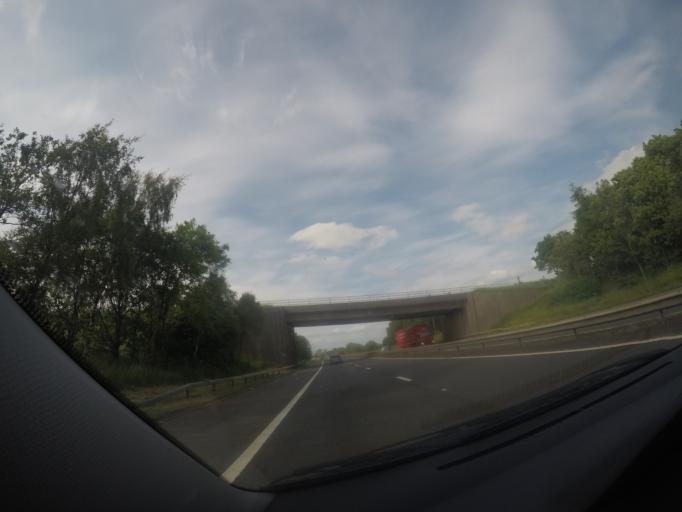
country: GB
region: Scotland
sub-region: North Lanarkshire
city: Glenboig
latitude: 55.8664
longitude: -4.0807
